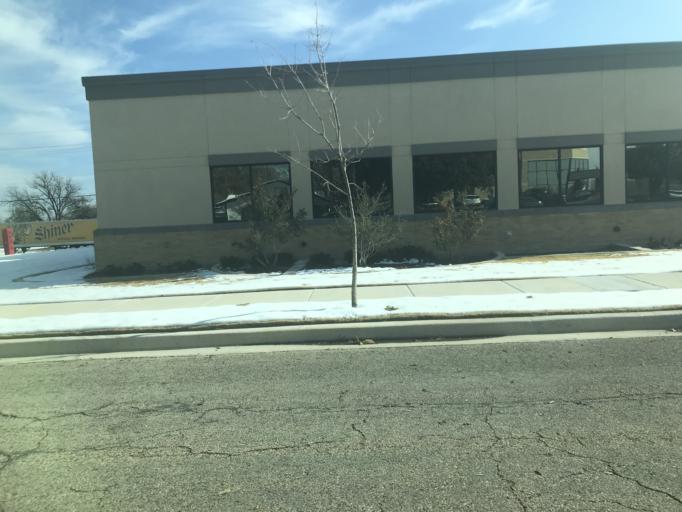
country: US
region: Texas
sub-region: Taylor County
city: Abilene
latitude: 32.4722
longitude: -99.7299
